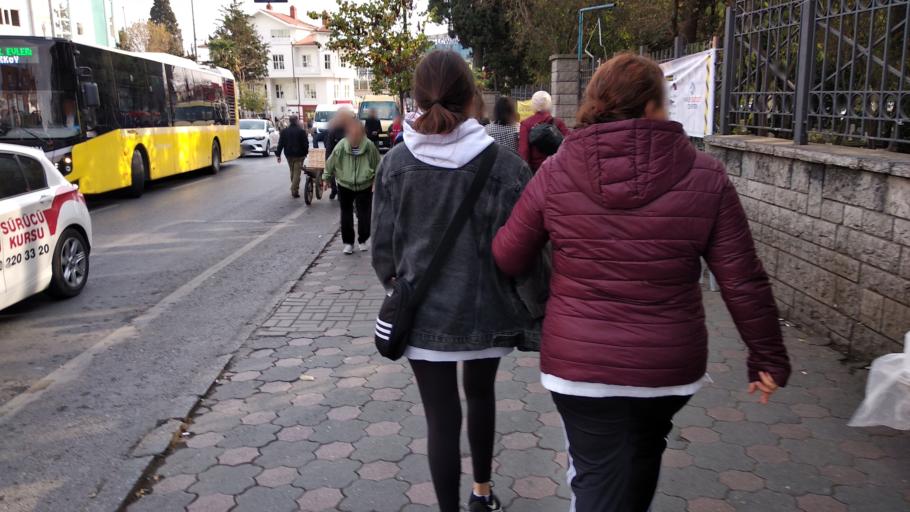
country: TR
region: Istanbul
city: Bahcelievler
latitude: 40.9821
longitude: 28.8733
